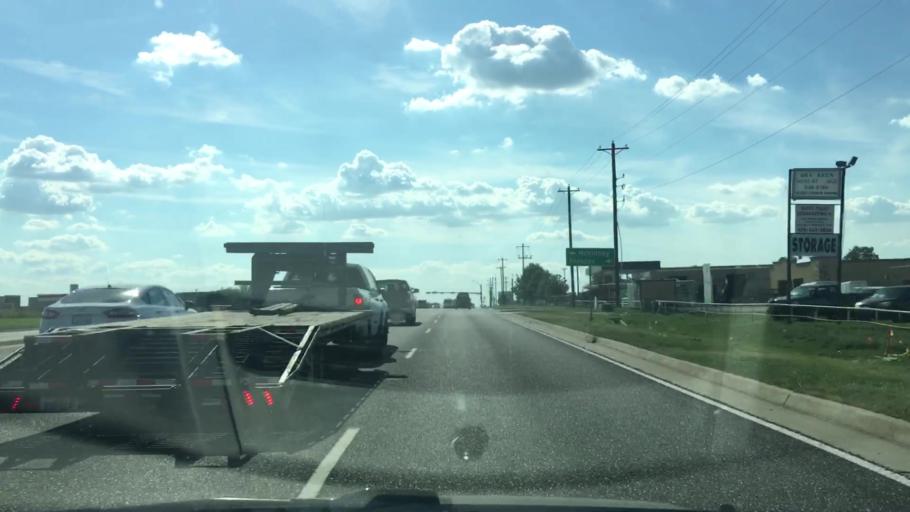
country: US
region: Texas
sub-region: Collin County
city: Prosper
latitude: 33.2188
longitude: -96.7297
